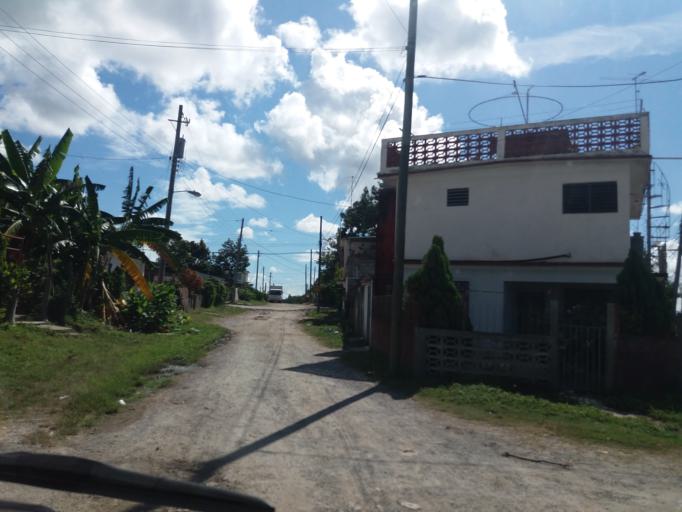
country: CU
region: Cienfuegos
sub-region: Municipio de Cienfuegos
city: Cienfuegos
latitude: 22.1469
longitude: -80.4239
